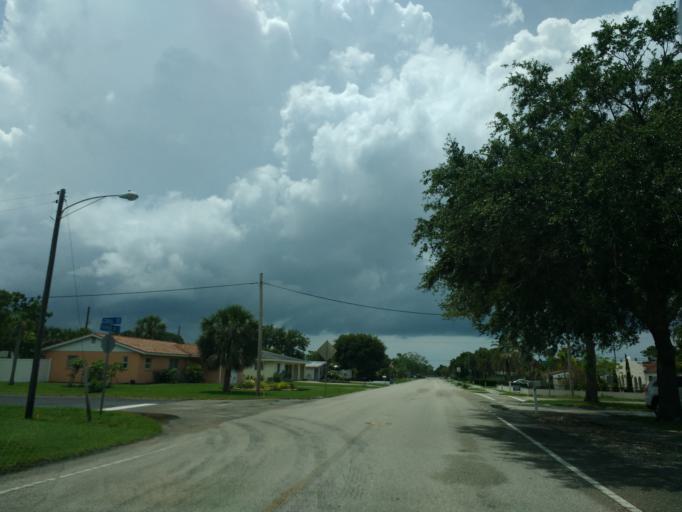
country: US
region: Florida
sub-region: Sarasota County
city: Venice
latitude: 27.0861
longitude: -82.4502
